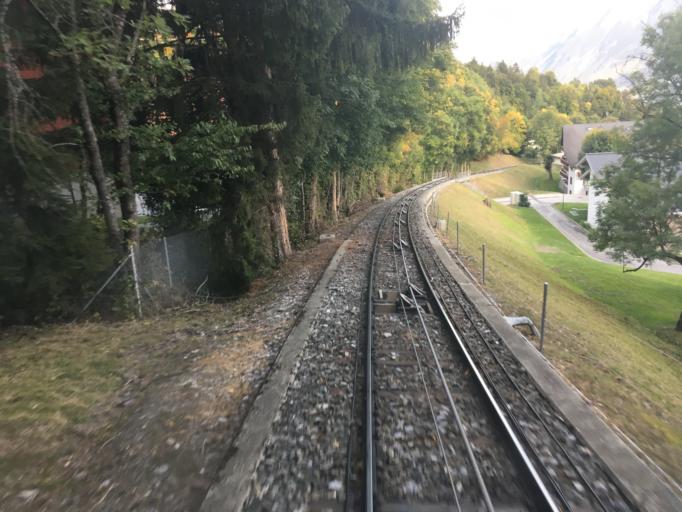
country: CH
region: Valais
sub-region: Sierre District
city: Randogne
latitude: 46.3121
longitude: 7.4965
